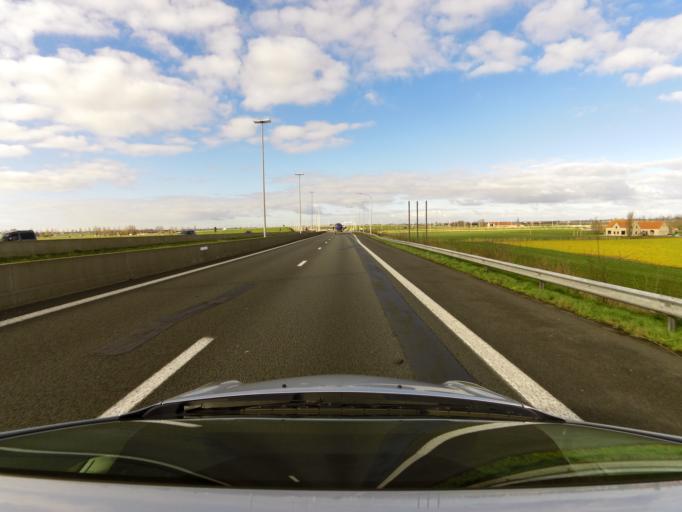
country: BE
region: Flanders
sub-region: Provincie West-Vlaanderen
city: Nieuwpoort
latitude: 51.1152
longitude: 2.7608
